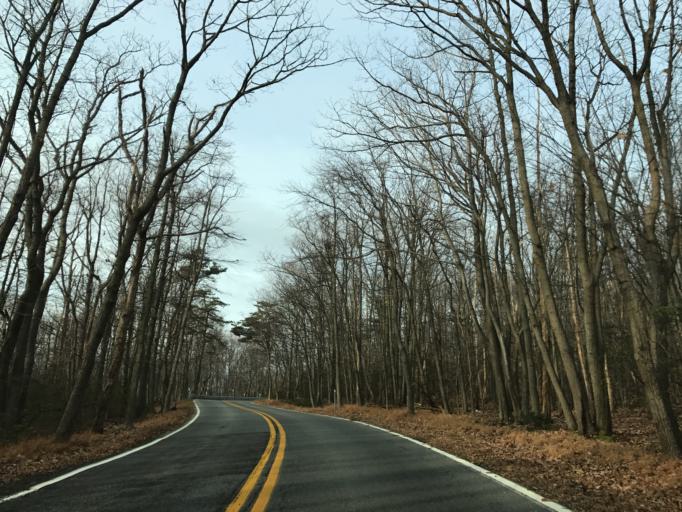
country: US
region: Maryland
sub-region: Frederick County
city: Middletown
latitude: 39.4917
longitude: -77.5003
